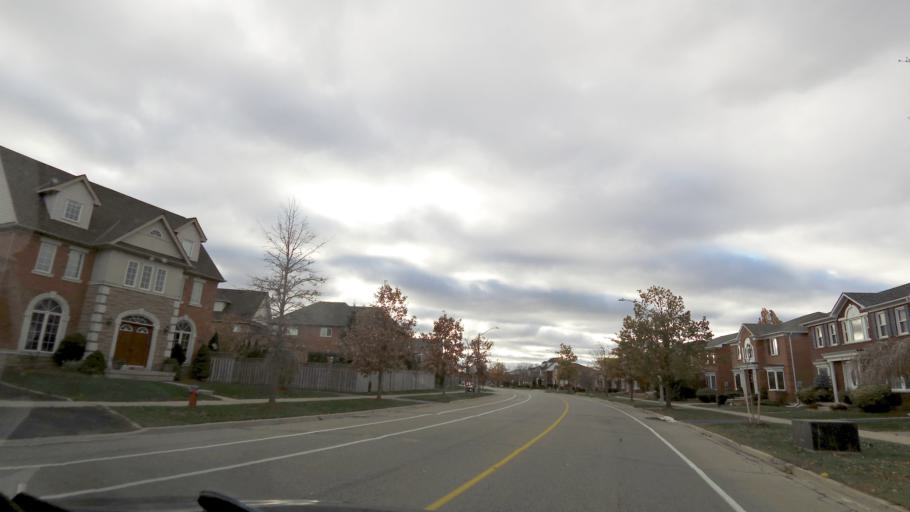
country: CA
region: Ontario
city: Oakville
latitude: 43.4740
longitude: -79.7303
